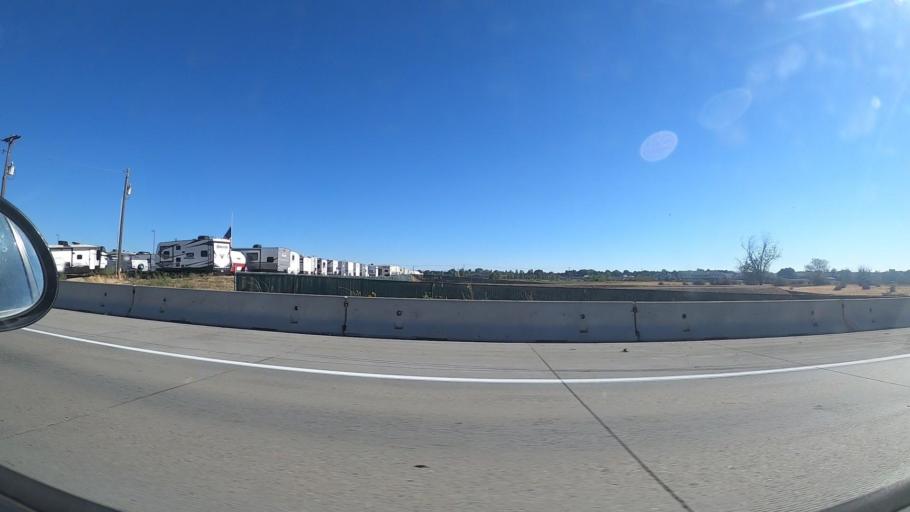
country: US
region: Idaho
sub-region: Ada County
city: Meridian
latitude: 43.5933
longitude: -116.4205
